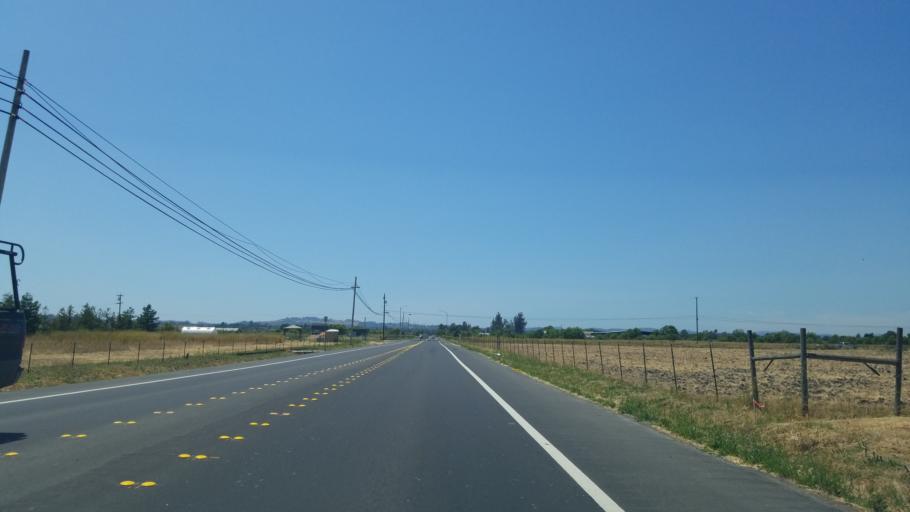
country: US
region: California
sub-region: Sonoma County
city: Rohnert Park
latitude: 38.3633
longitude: -122.7271
